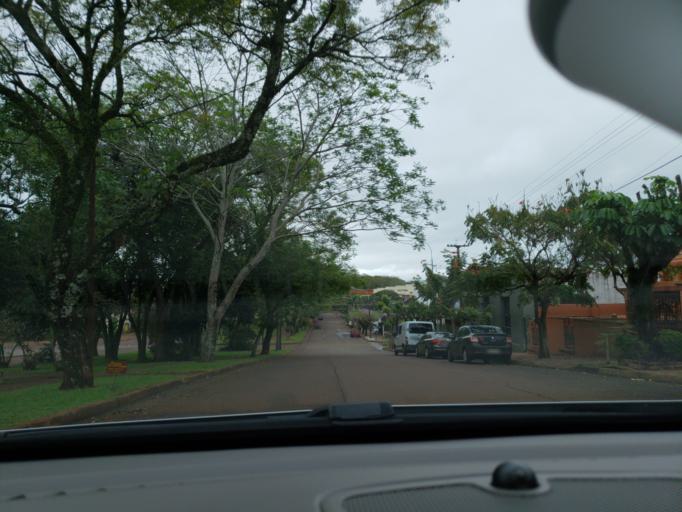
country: AR
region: Misiones
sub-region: Departamento de Apostoles
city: Apostoles
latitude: -27.9118
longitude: -55.7526
